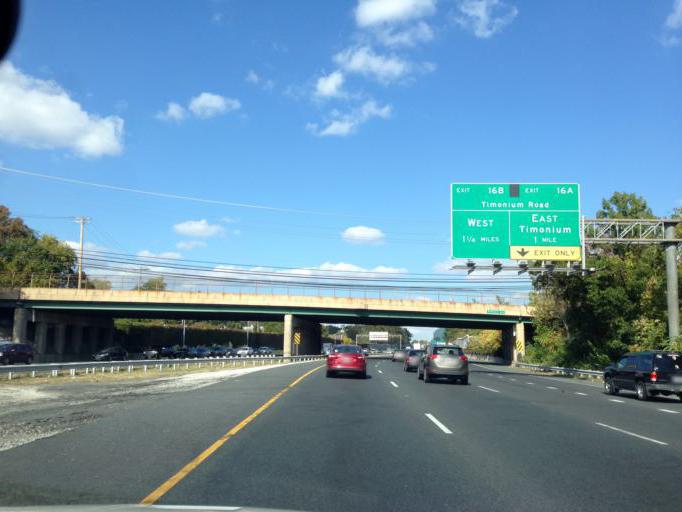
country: US
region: Maryland
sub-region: Baltimore County
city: Lutherville
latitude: 39.4232
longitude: -76.6381
